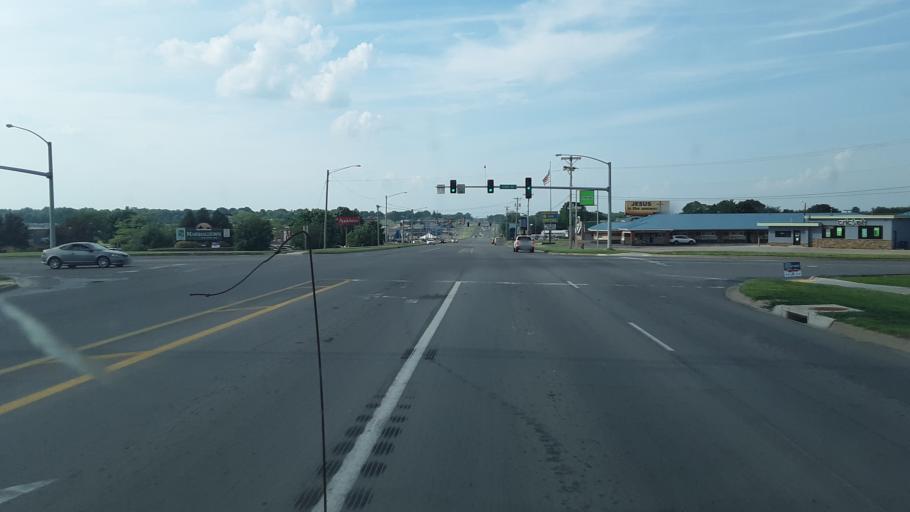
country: US
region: Iowa
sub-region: Marshall County
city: Marshalltown
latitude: 42.0066
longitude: -92.9123
